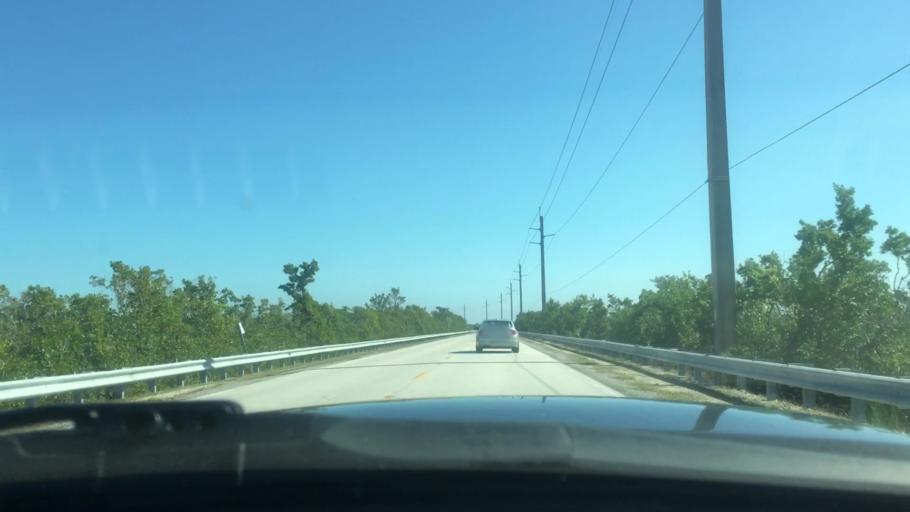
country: US
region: Florida
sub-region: Monroe County
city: North Key Largo
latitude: 25.2840
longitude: -80.3172
